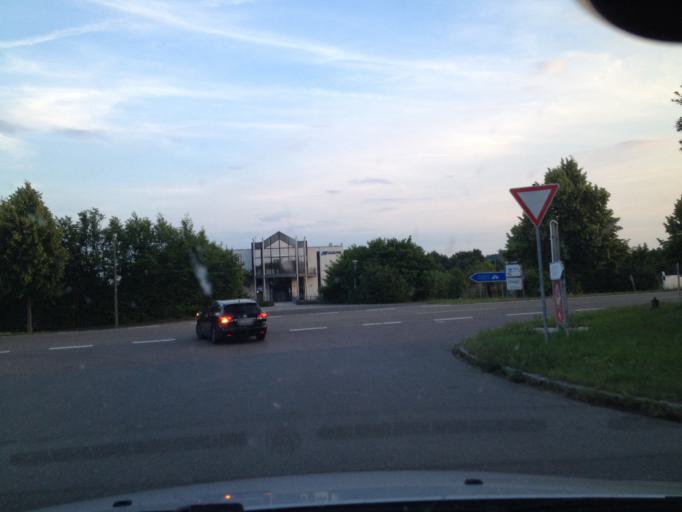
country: DE
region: Bavaria
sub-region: Regierungsbezirk Mittelfranken
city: Schillingsfurst
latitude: 49.2581
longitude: 10.2338
